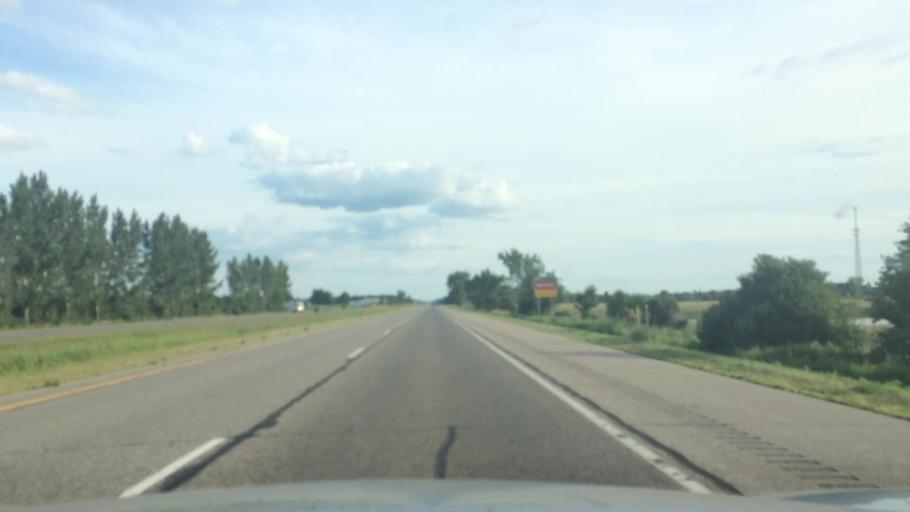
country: US
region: Wisconsin
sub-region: Portage County
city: Plover
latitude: 44.3272
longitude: -89.5235
